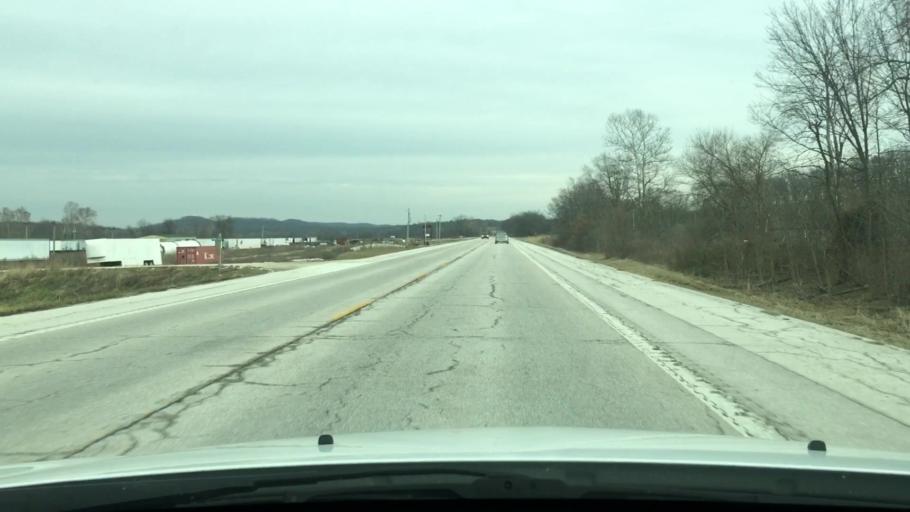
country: US
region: Missouri
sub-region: Pike County
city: Bowling Green
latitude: 39.3821
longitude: -91.1337
